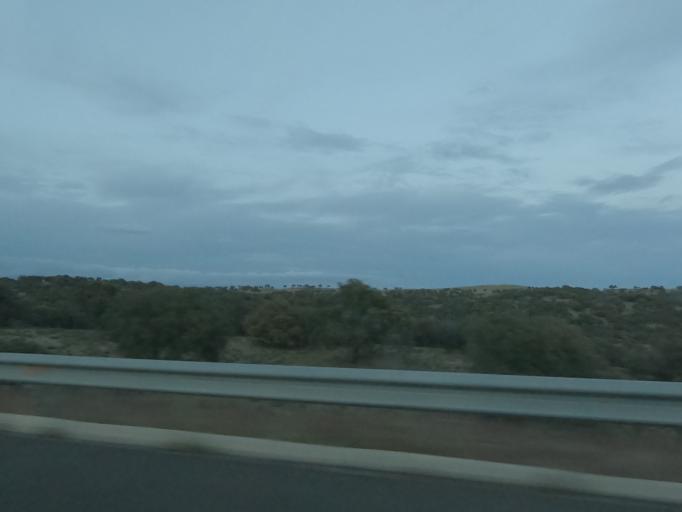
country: ES
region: Extremadura
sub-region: Provincia de Caceres
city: Casar de Caceres
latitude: 39.6036
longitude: -6.4062
